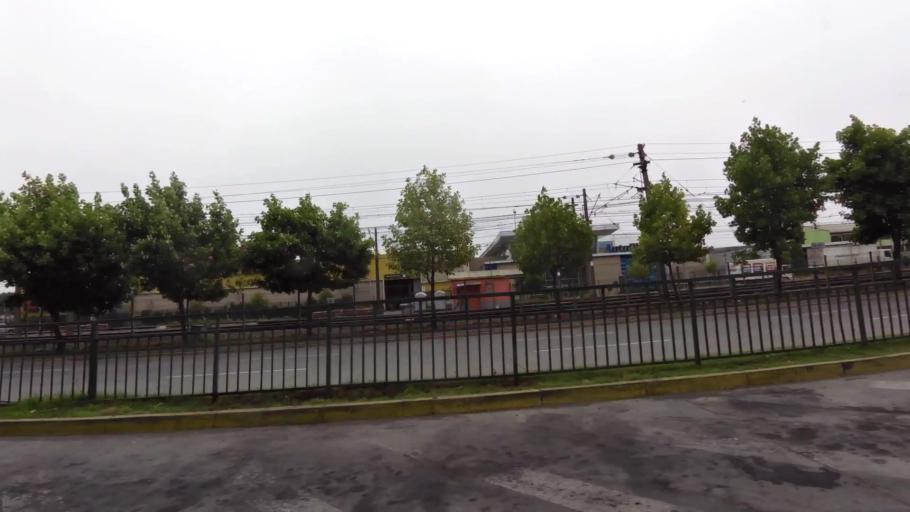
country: CL
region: Biobio
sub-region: Provincia de Concepcion
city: Concepcion
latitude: -36.8287
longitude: -73.0616
